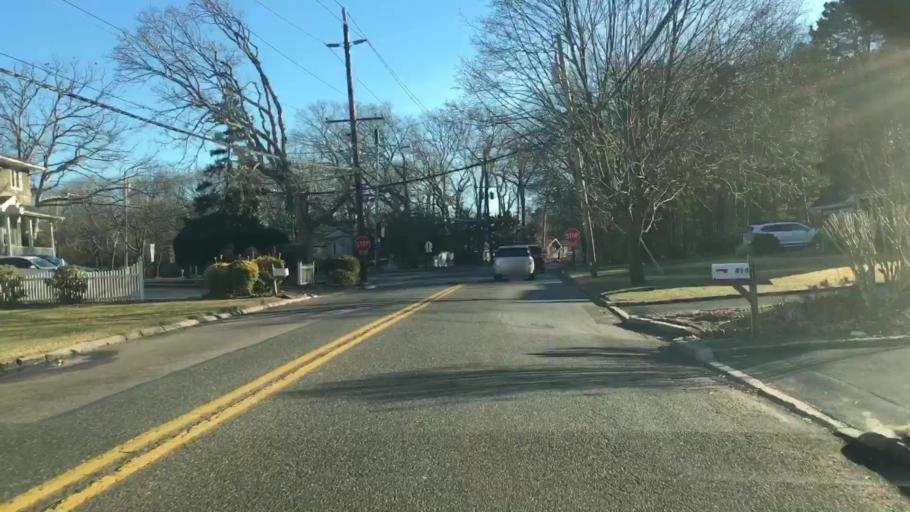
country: US
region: New York
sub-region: Suffolk County
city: Lake Ronkonkoma
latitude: 40.8384
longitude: -73.1357
